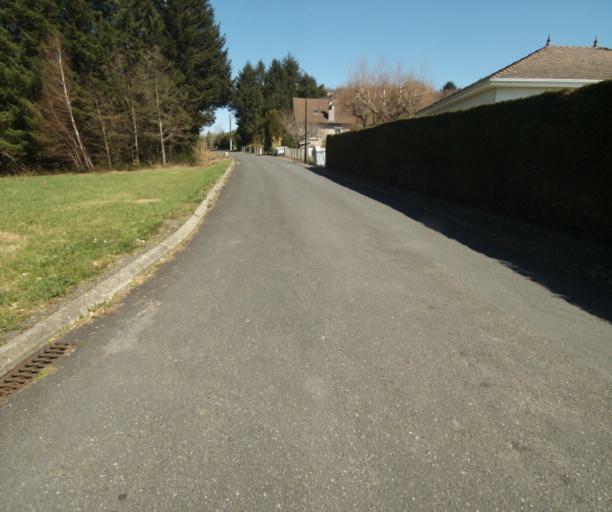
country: FR
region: Limousin
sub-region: Departement de la Correze
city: Saint-Mexant
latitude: 45.2799
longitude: 1.6606
